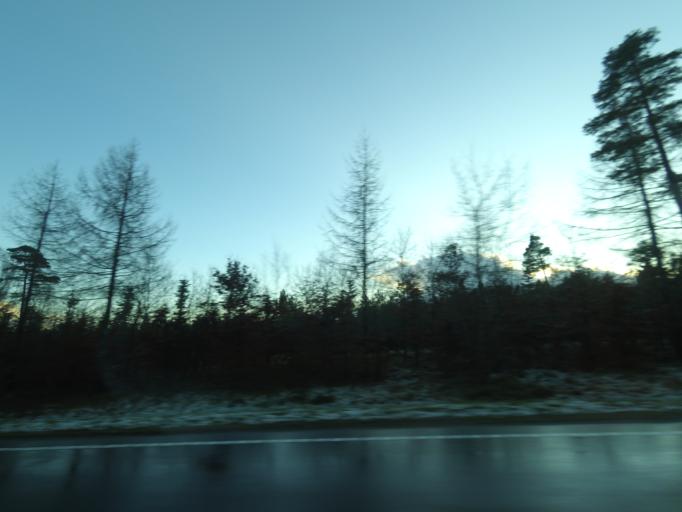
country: DK
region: Central Jutland
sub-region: Ikast-Brande Kommune
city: Brande
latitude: 56.0106
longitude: 9.0550
